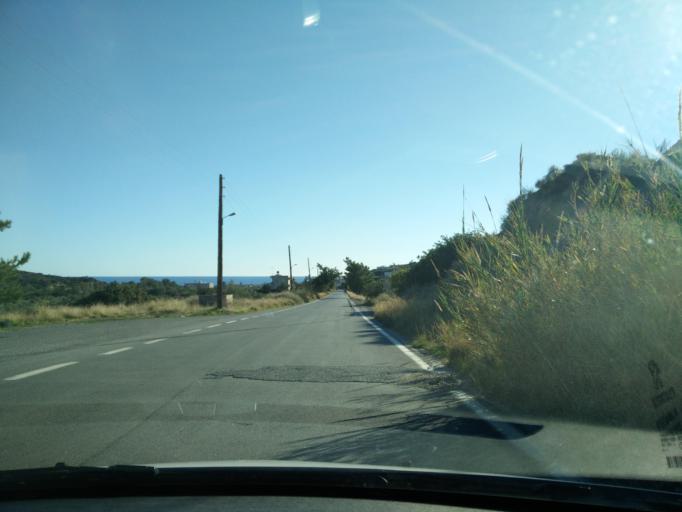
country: GR
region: Crete
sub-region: Nomos Lasithiou
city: Gra Liyia
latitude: 35.0146
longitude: 25.5834
